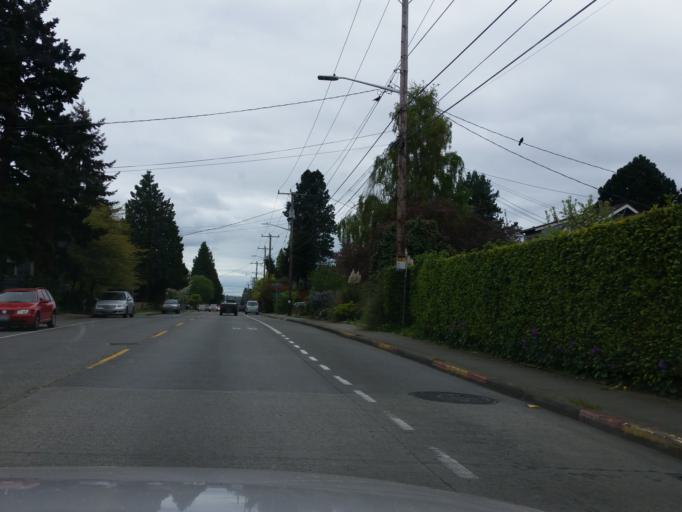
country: US
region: Washington
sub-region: King County
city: Shoreline
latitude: 47.6942
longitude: -122.3661
